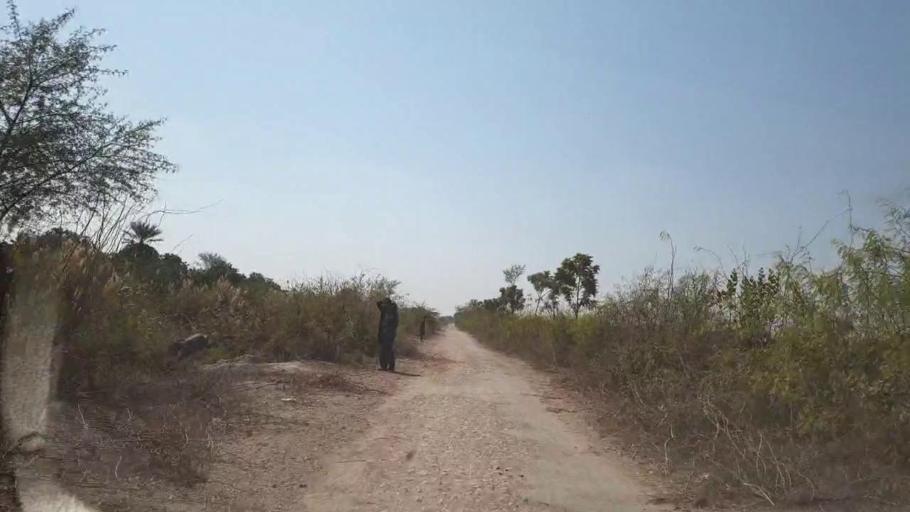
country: PK
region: Sindh
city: Mirpur Khas
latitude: 25.7229
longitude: 69.1070
